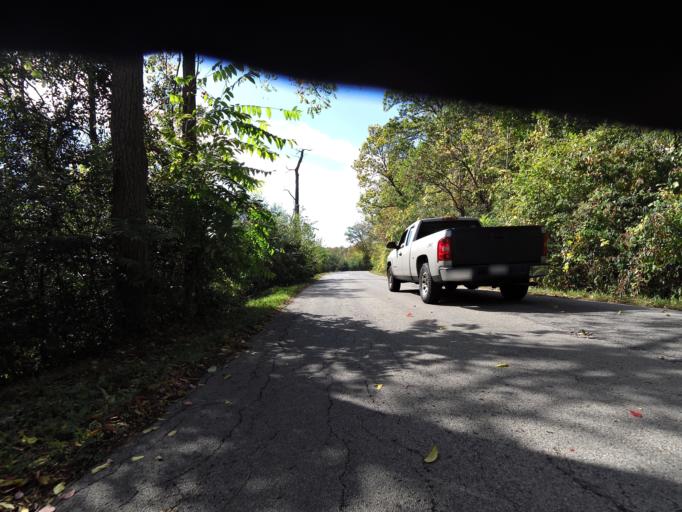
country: CA
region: Ontario
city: Hamilton
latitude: 43.2993
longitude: -79.9233
